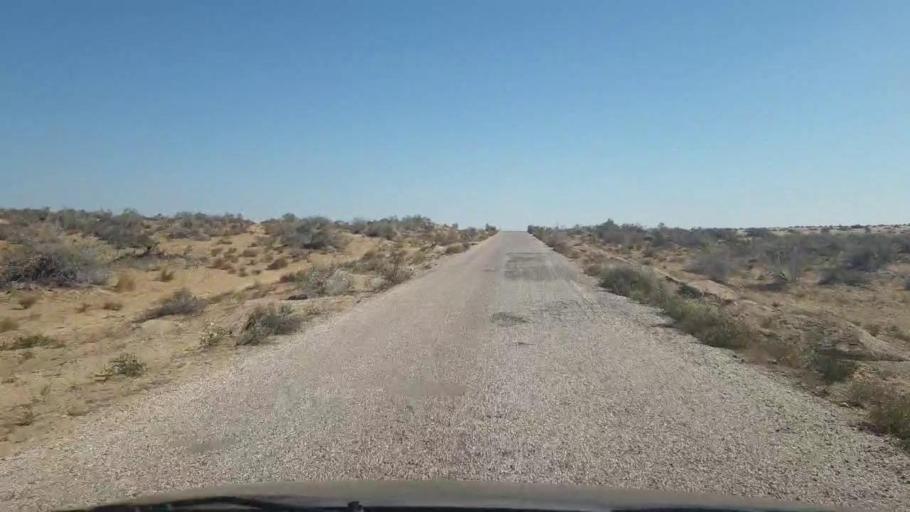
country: PK
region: Sindh
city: Bozdar
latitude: 26.9993
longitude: 68.8538
